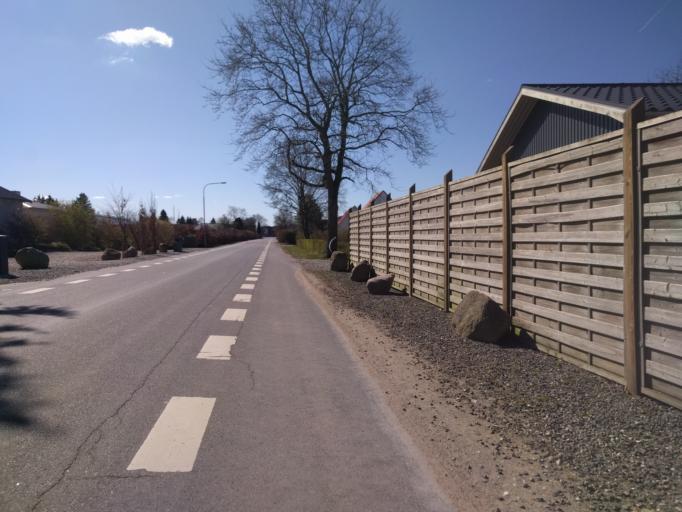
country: DK
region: South Denmark
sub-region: Kerteminde Kommune
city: Langeskov
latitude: 55.3770
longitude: 10.5589
